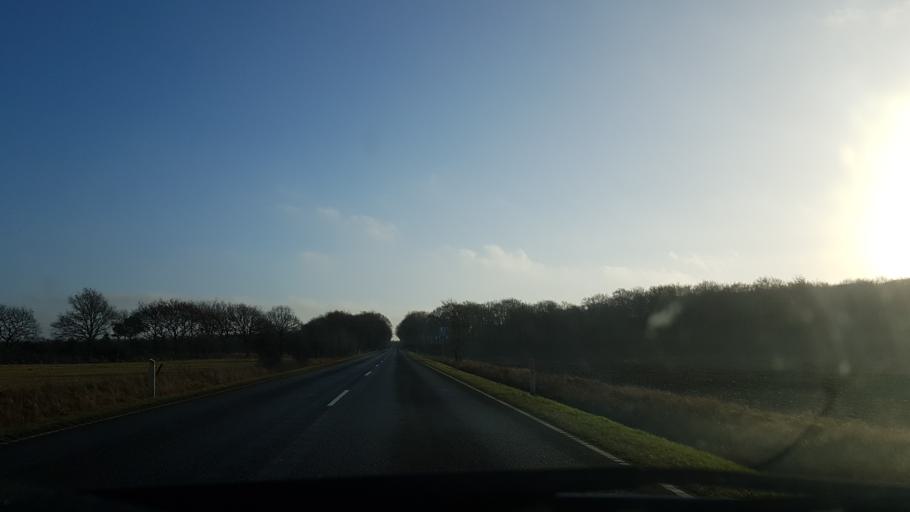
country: DK
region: South Denmark
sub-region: Tonder Kommune
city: Toftlund
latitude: 55.2253
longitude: 9.1745
